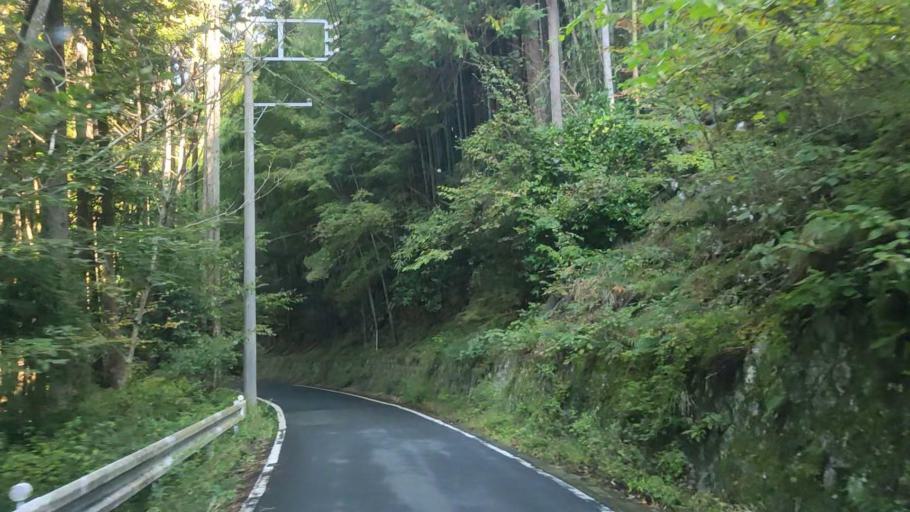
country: JP
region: Shizuoka
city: Ito
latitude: 34.9486
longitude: 139.0018
